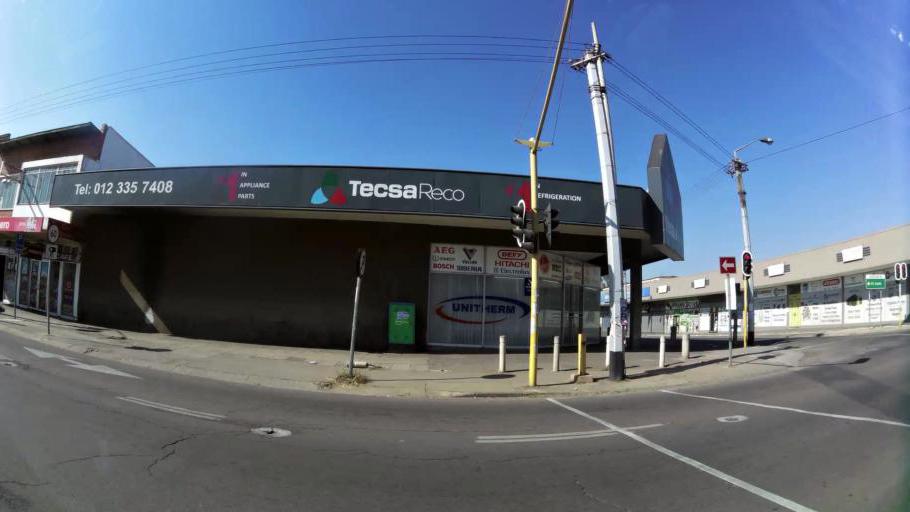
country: ZA
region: Gauteng
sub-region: City of Tshwane Metropolitan Municipality
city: Pretoria
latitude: -25.7184
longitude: 28.2025
